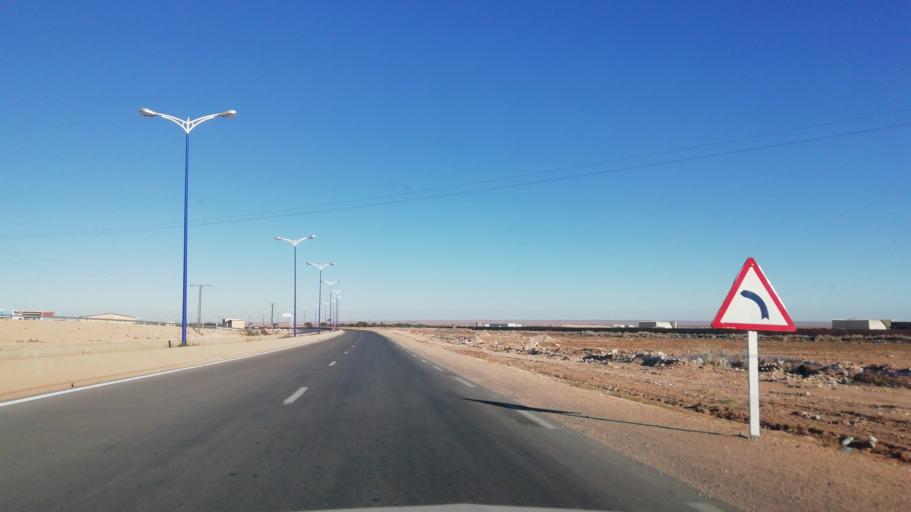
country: DZ
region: Wilaya de Naama
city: Naama
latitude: 33.5397
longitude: -0.2588
